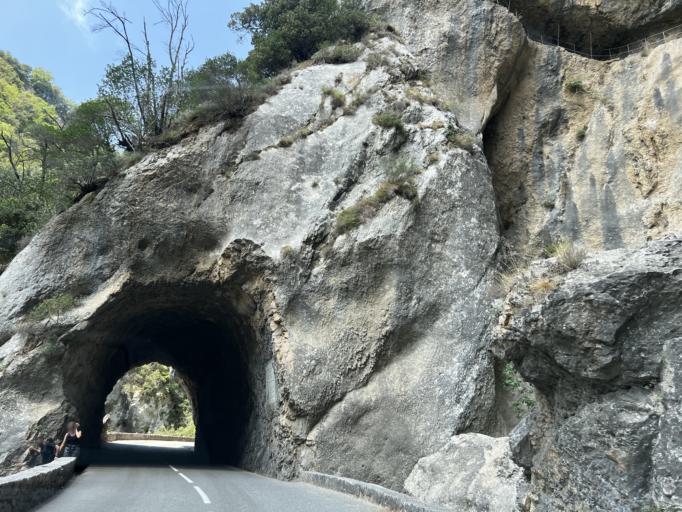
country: FR
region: Provence-Alpes-Cote d'Azur
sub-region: Departement des Alpes-Maritimes
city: Tourrettes-sur-Loup
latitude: 43.7418
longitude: 7.0005
